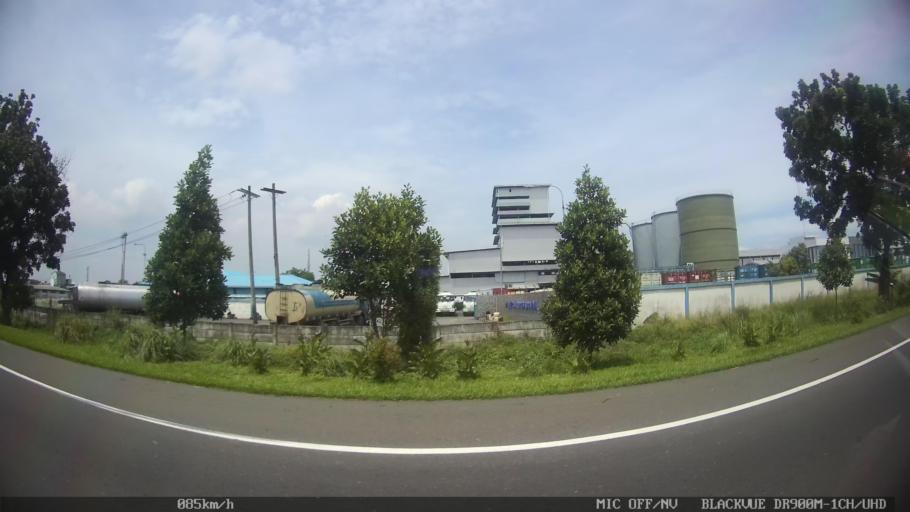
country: ID
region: North Sumatra
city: Labuhan Deli
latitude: 3.7246
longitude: 98.6821
